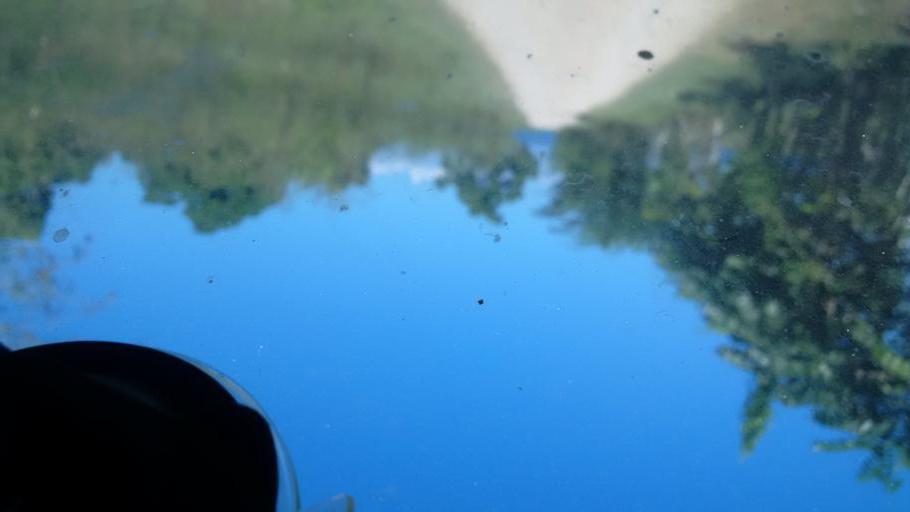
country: HT
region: Ouest
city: Grangwav
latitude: 18.4292
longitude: -72.7905
